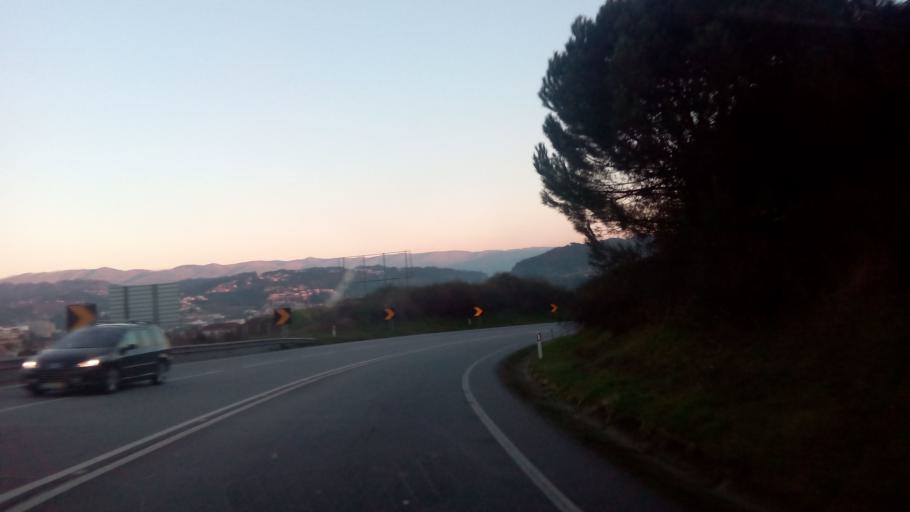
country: PT
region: Porto
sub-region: Amarante
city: Amarante
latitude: 41.2694
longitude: -8.0928
